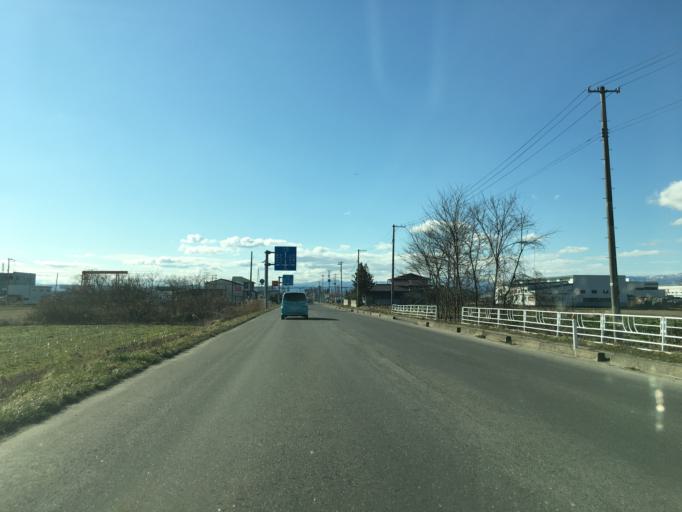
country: JP
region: Yamagata
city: Takahata
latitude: 38.0059
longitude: 140.1504
